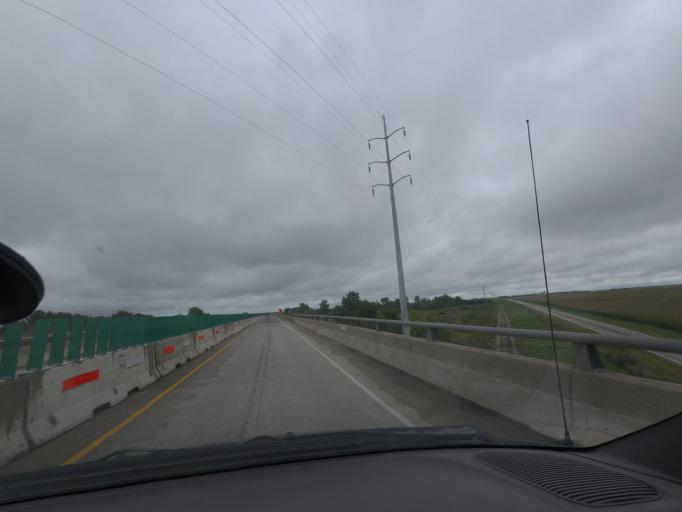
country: US
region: Illinois
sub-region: Piatt County
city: Cerro Gordo
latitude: 39.9982
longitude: -88.7802
